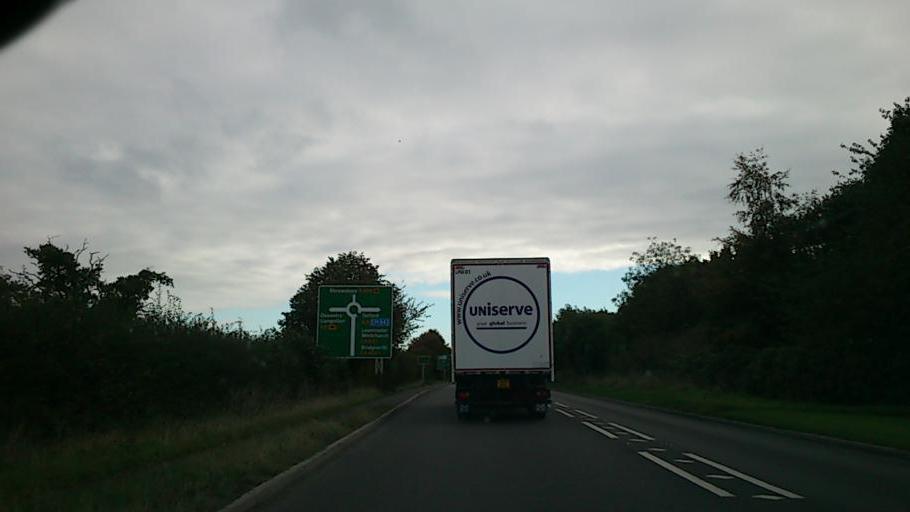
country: GB
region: England
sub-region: Shropshire
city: Bicton
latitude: 52.7164
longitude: -2.8231
